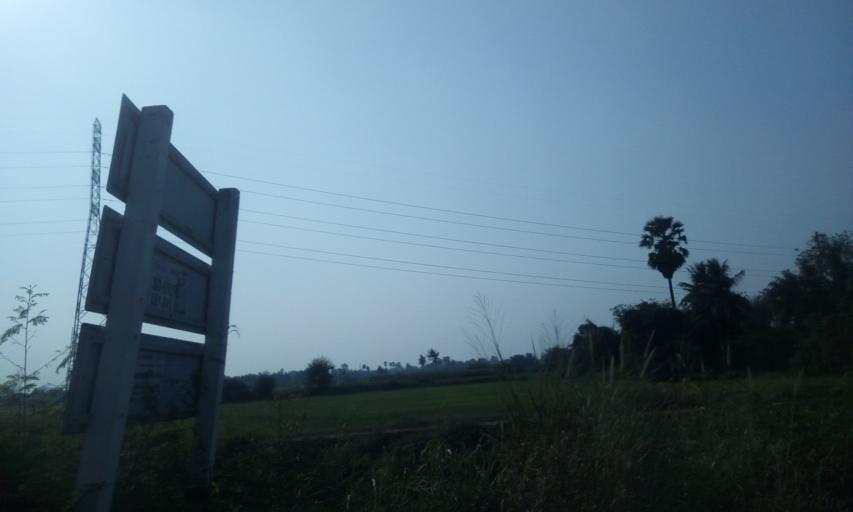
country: TH
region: Sing Buri
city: Tha Chang
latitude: 14.7272
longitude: 100.4300
